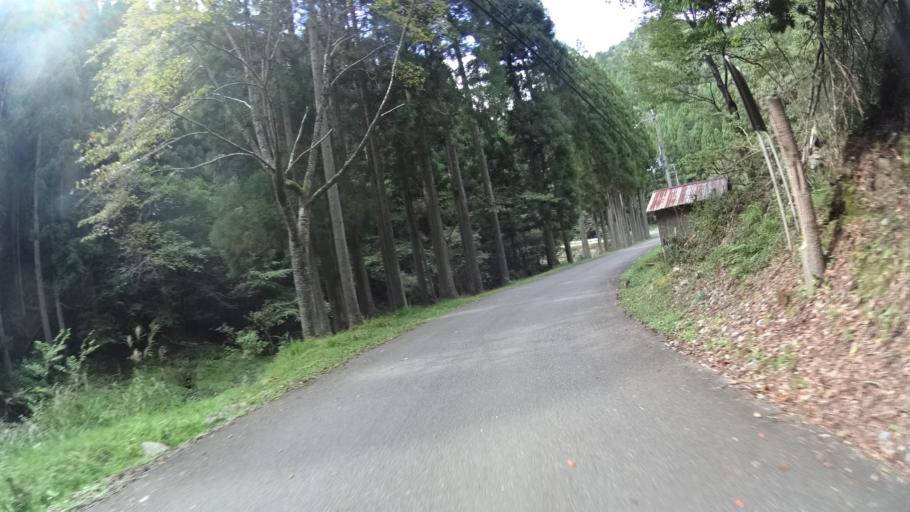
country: JP
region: Shiga Prefecture
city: Kitahama
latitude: 35.2322
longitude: 135.7911
